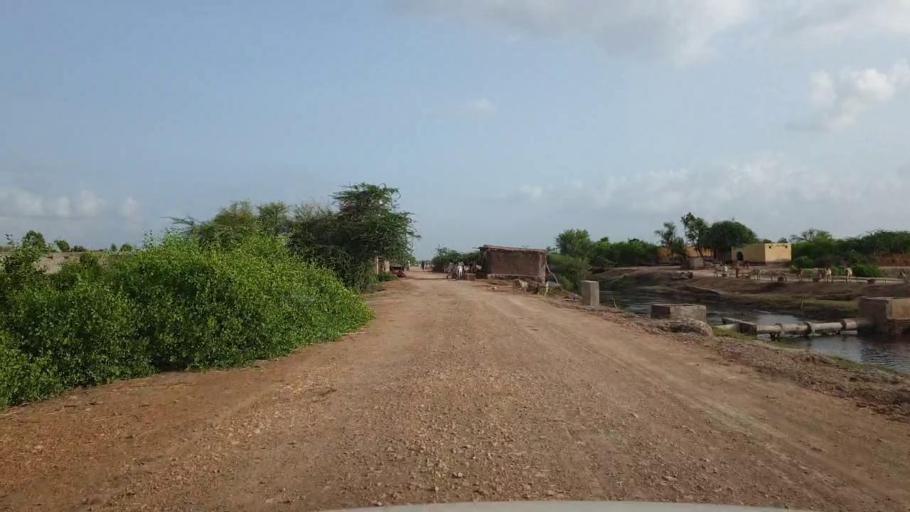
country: PK
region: Sindh
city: Kario
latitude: 24.8593
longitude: 68.6520
